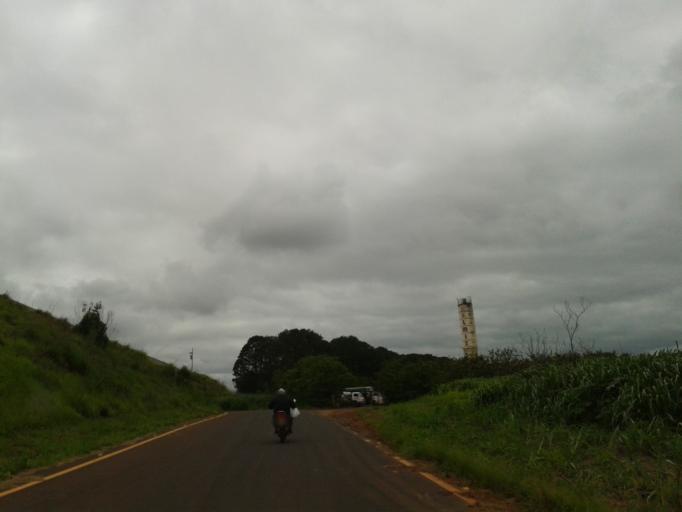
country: BR
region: Minas Gerais
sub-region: Uberlandia
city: Uberlandia
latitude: -18.9379
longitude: -48.2131
